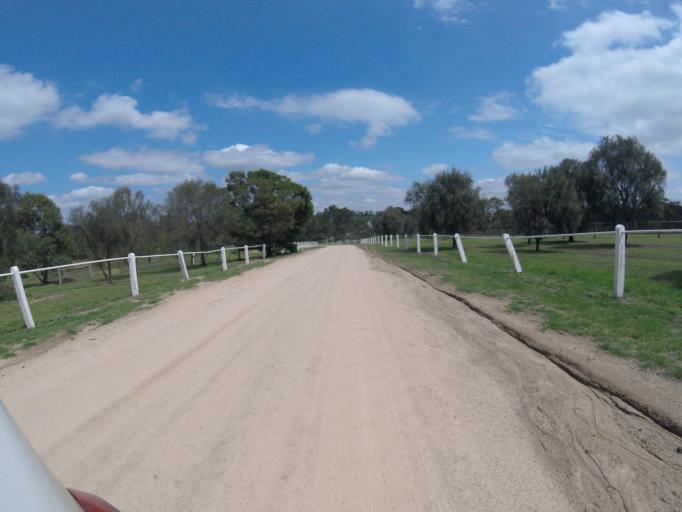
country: AU
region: Victoria
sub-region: Hume
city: Greenvale
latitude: -37.6407
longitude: 144.8391
